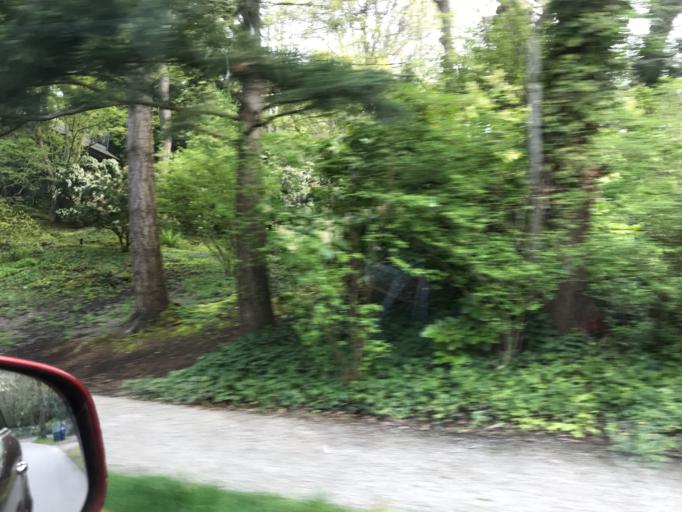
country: US
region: Washington
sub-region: King County
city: Seattle
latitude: 47.6240
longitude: -122.2879
